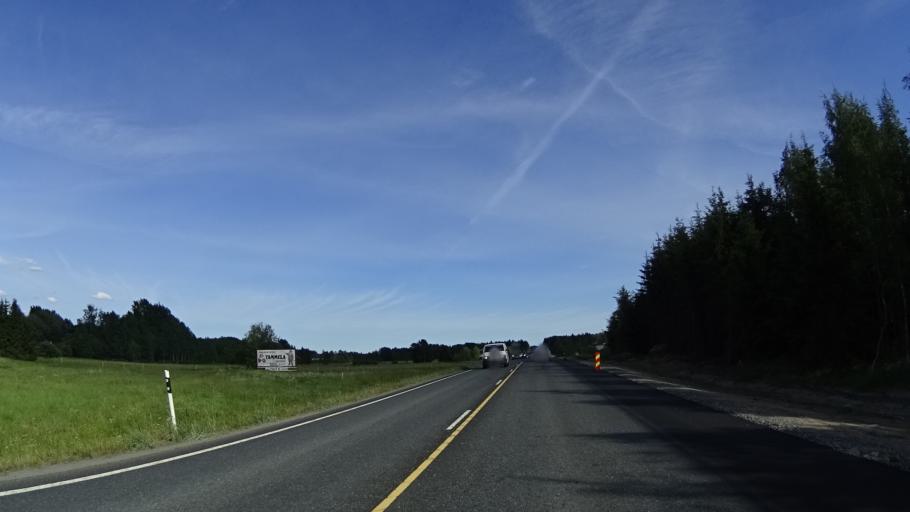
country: FI
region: Haeme
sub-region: Forssa
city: Tammela
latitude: 60.7592
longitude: 23.6985
